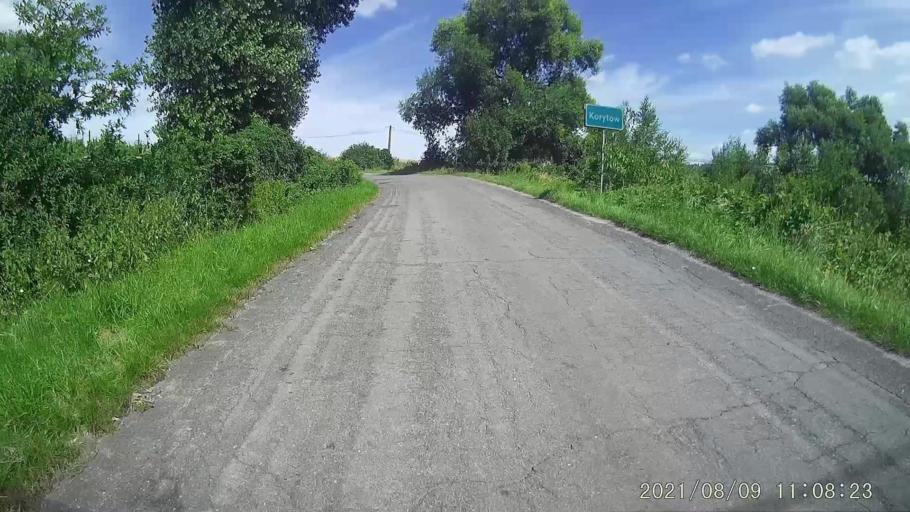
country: PL
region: Lower Silesian Voivodeship
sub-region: Powiat klodzki
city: Klodzko
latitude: 50.4554
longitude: 16.6087
